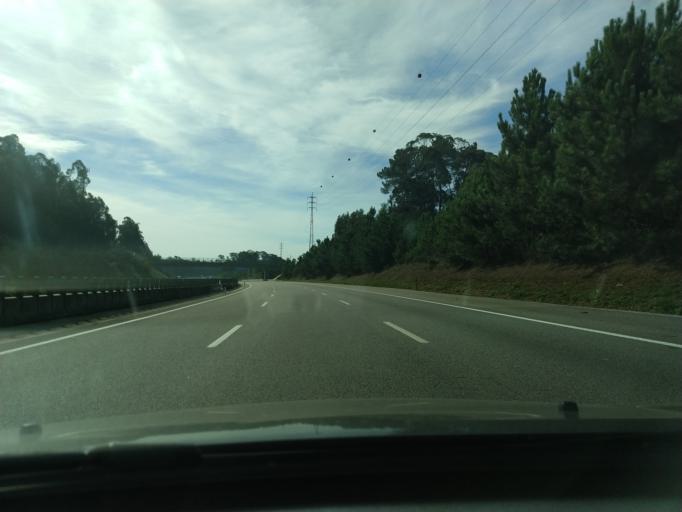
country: PT
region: Aveiro
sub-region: Ovar
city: Valega
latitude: 40.8475
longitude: -8.5576
